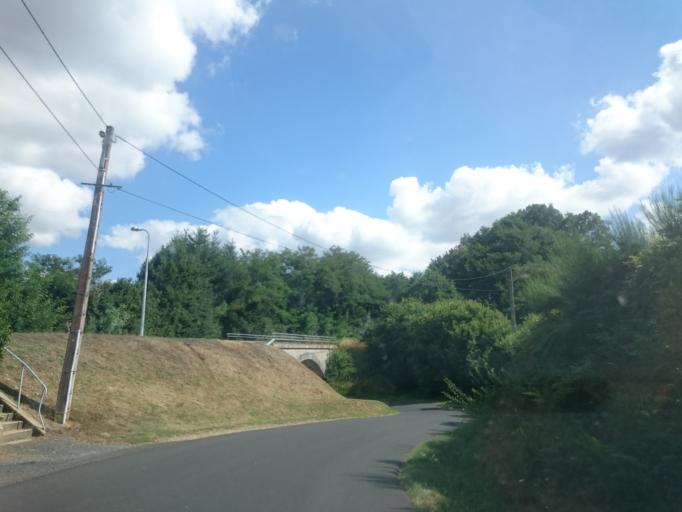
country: FR
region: Auvergne
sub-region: Departement du Cantal
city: Saint-Mamet-la-Salvetat
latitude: 44.8868
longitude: 2.2402
